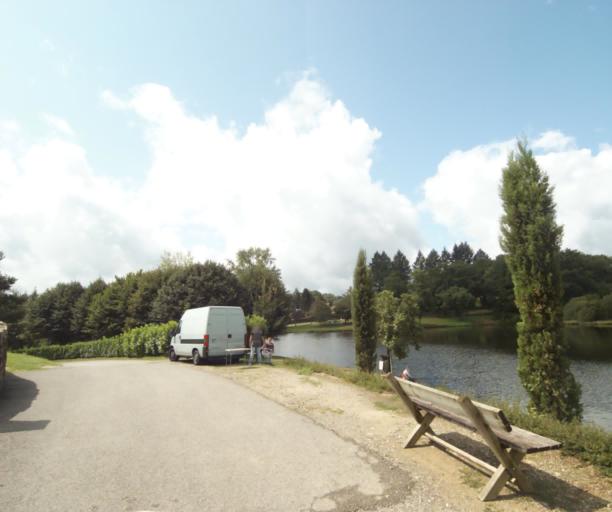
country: FR
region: Limousin
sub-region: Departement de la Correze
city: Sainte-Fortunade
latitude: 45.1865
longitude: 1.8020
